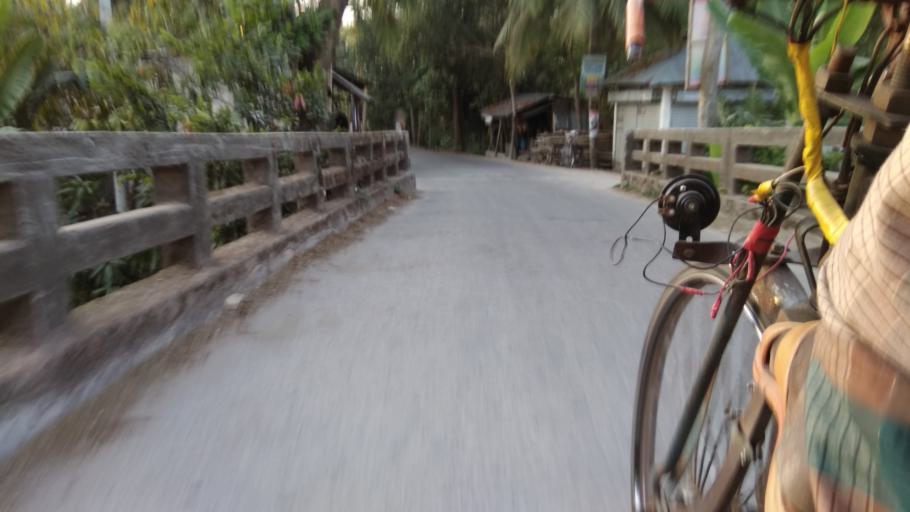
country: BD
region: Barisal
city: Mehendiganj
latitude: 22.9256
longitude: 90.4051
